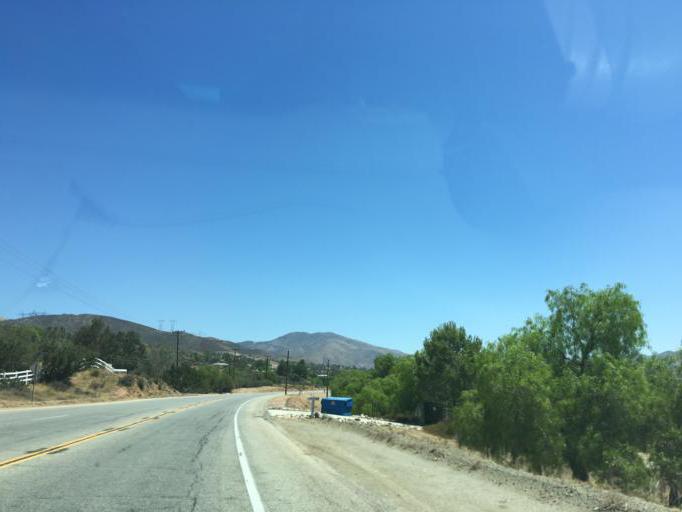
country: US
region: California
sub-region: Los Angeles County
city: Agua Dulce
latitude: 34.5193
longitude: -118.3221
